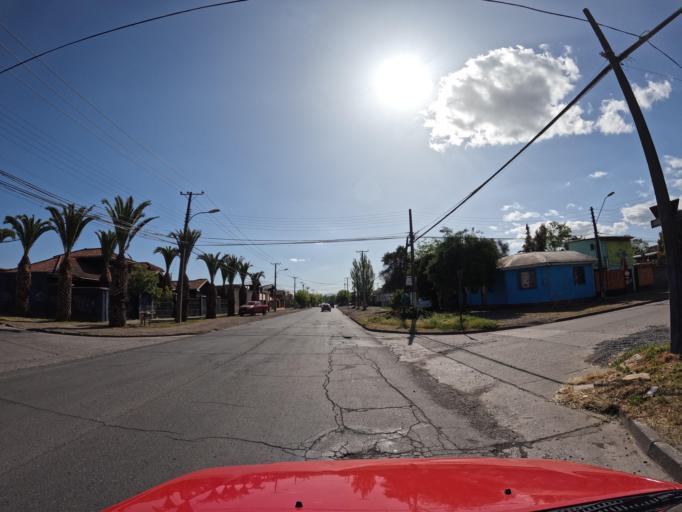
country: CL
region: Maule
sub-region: Provincia de Curico
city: Curico
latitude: -34.9760
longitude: -71.2511
